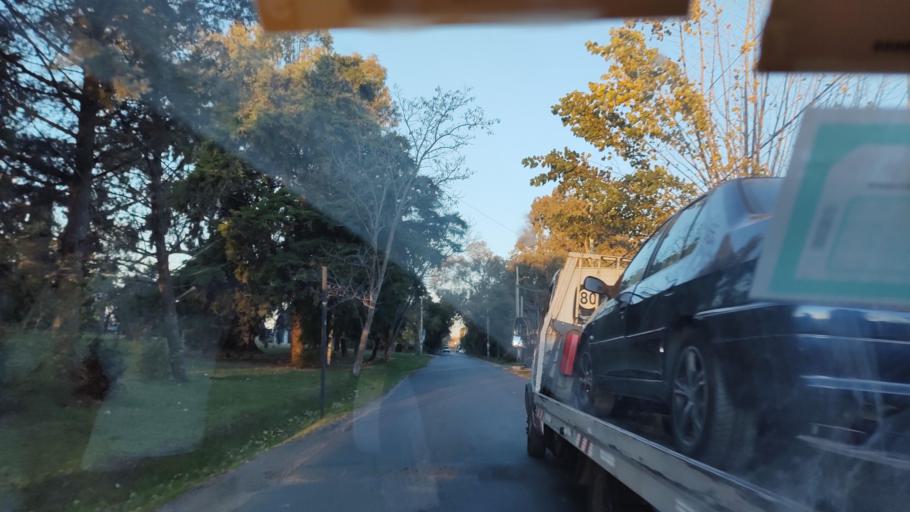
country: AR
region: Buenos Aires
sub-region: Partido de La Plata
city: La Plata
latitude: -34.9053
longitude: -58.0395
